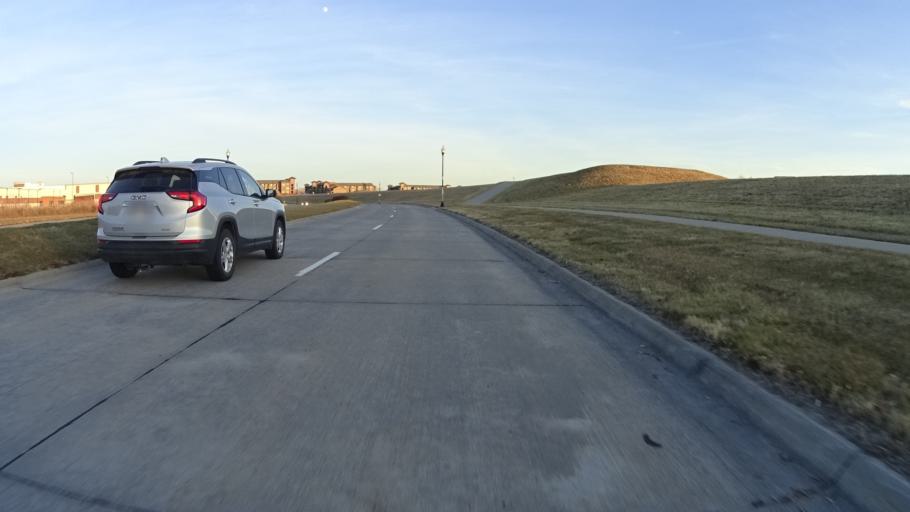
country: US
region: Nebraska
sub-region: Sarpy County
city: Papillion
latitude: 41.1323
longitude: -96.0325
